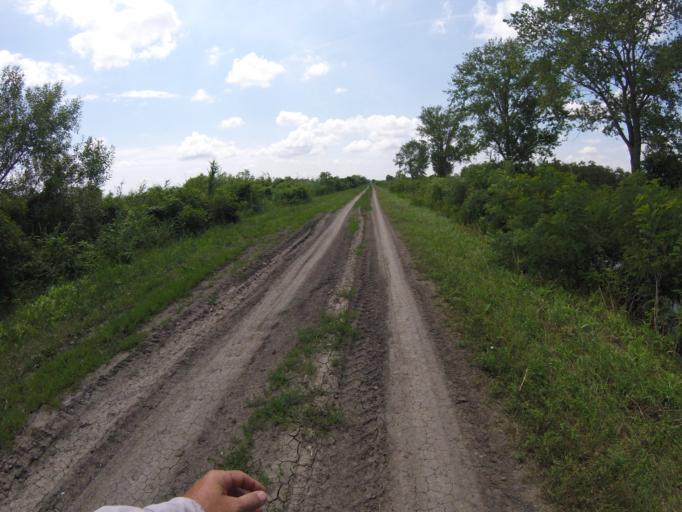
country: HU
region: Hajdu-Bihar
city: Hortobagy
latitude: 47.6332
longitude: 21.0821
